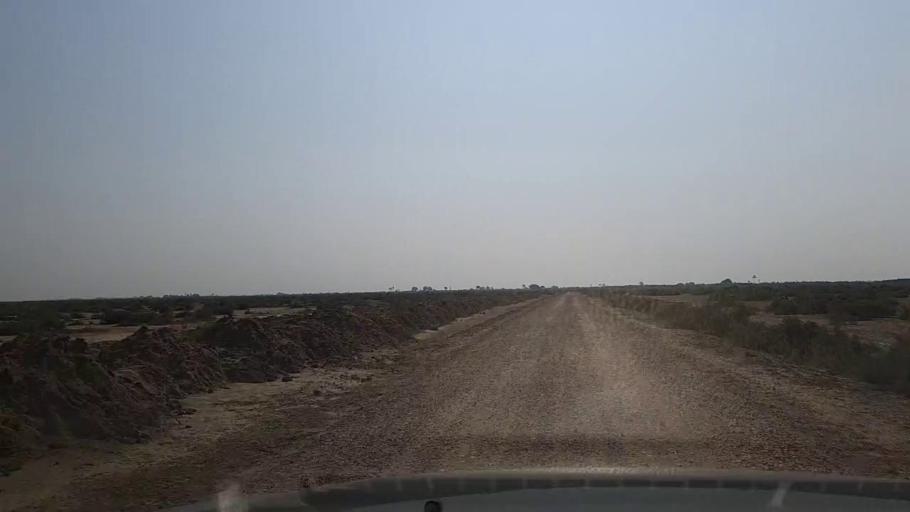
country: PK
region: Sindh
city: Mirpur Sakro
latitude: 24.4289
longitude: 67.7183
